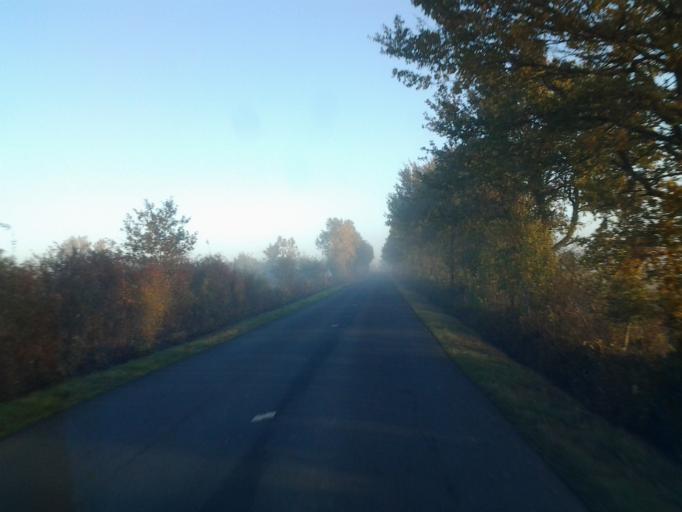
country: FR
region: Pays de la Loire
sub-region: Departement de la Vendee
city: Bournezeau
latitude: 46.6443
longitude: -1.2317
